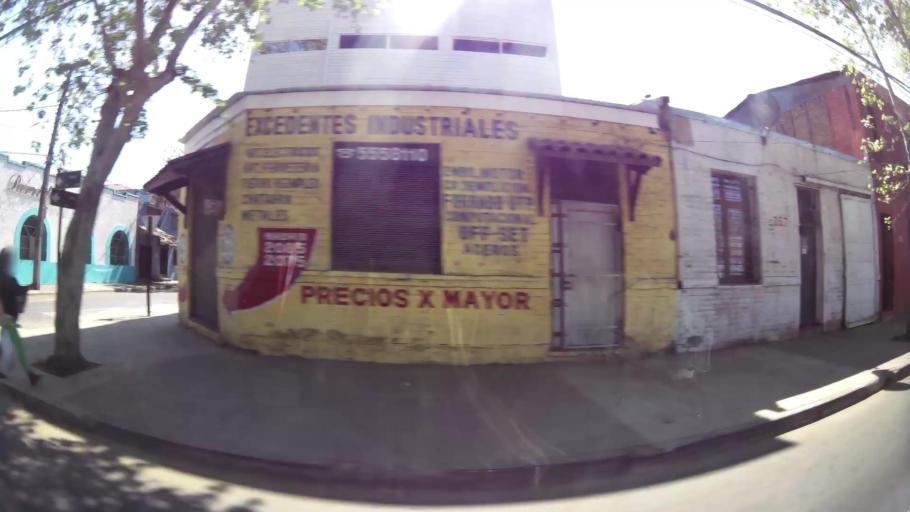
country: CL
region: Santiago Metropolitan
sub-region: Provincia de Santiago
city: Santiago
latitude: -33.4720
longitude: -70.6315
